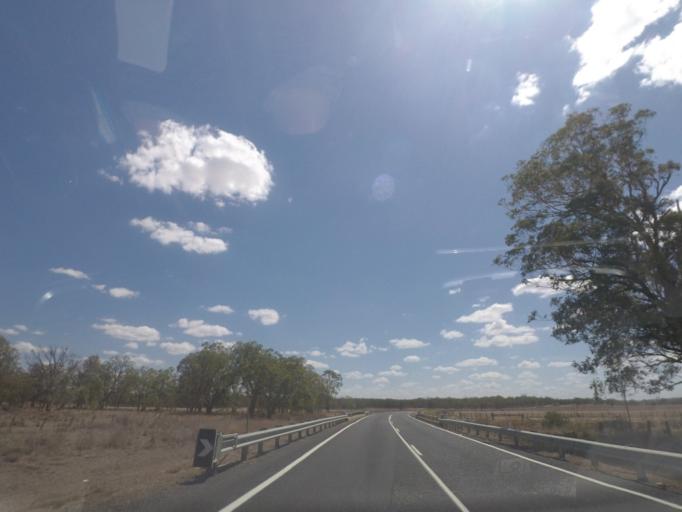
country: AU
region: Queensland
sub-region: Southern Downs
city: Warwick
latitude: -28.1830
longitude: 151.8174
